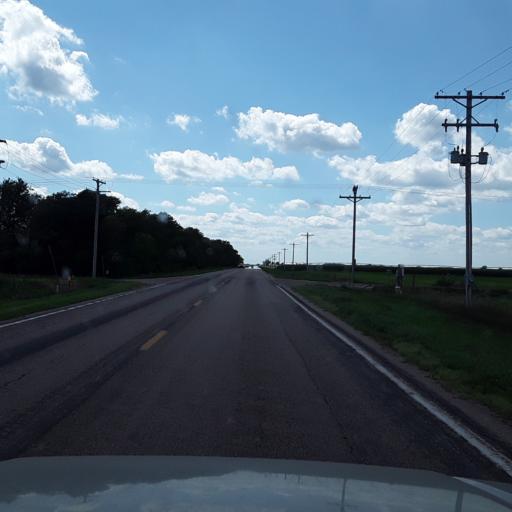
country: US
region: Nebraska
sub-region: Merrick County
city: Central City
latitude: 41.1910
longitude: -98.0204
